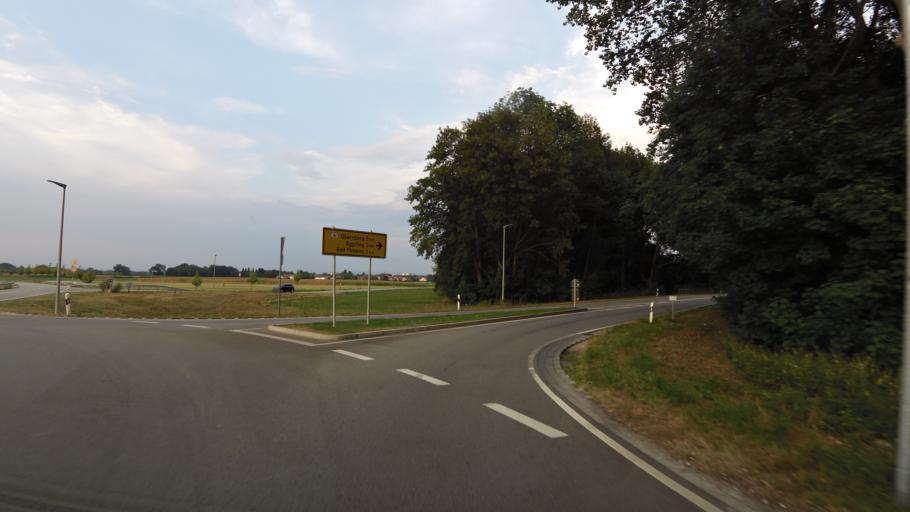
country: DE
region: Bavaria
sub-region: Lower Bavaria
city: Bad Fussing
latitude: 48.3484
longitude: 13.2931
